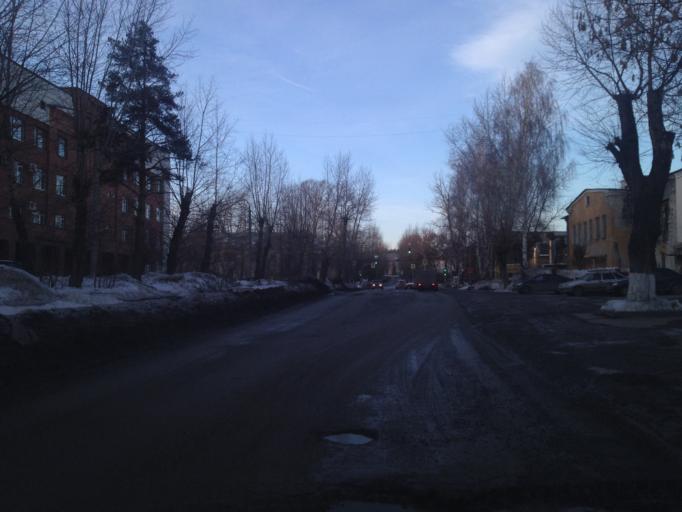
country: RU
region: Sverdlovsk
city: Istok
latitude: 56.7576
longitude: 60.7105
